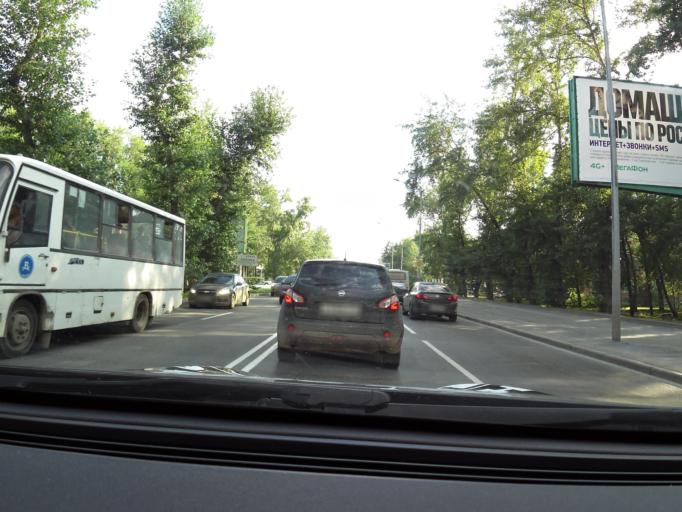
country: RU
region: Sverdlovsk
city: Yekaterinburg
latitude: 56.8342
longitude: 60.5785
